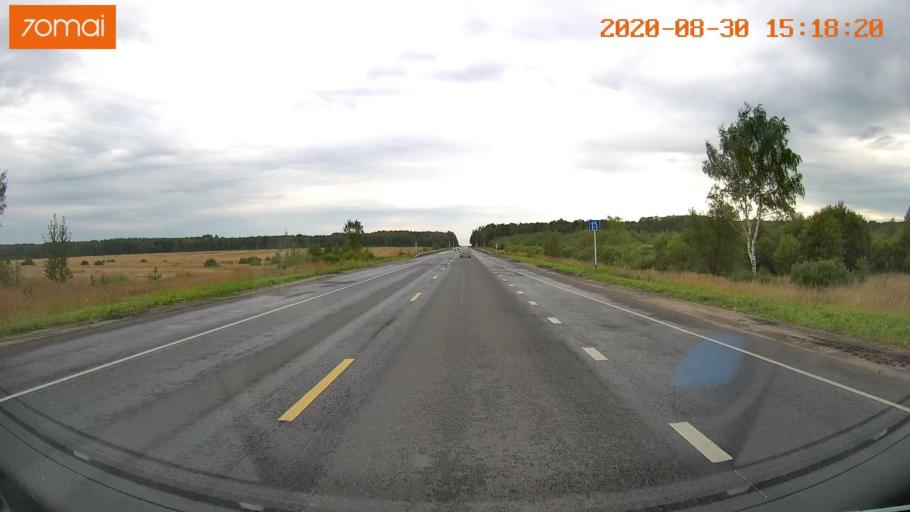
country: RU
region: Ivanovo
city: Rodniki
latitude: 57.1243
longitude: 41.7947
